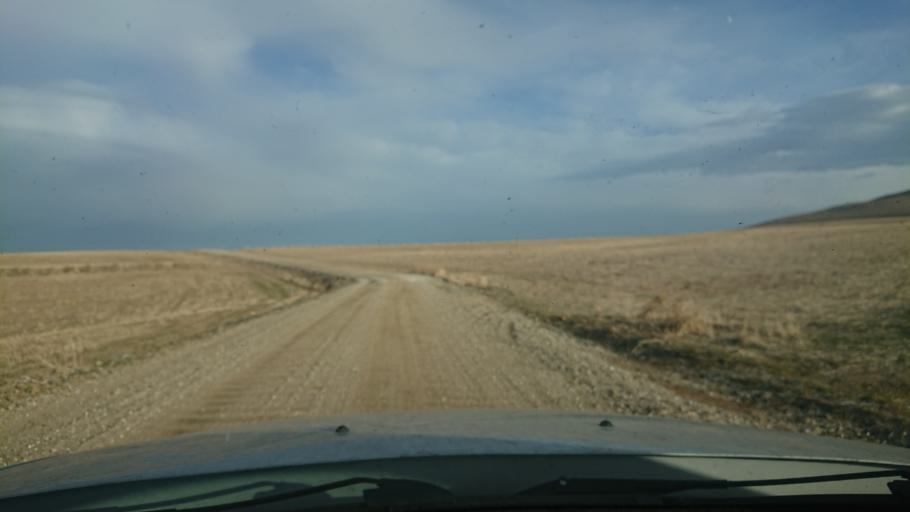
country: TR
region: Aksaray
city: Ortakoy
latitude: 38.7018
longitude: 33.8732
